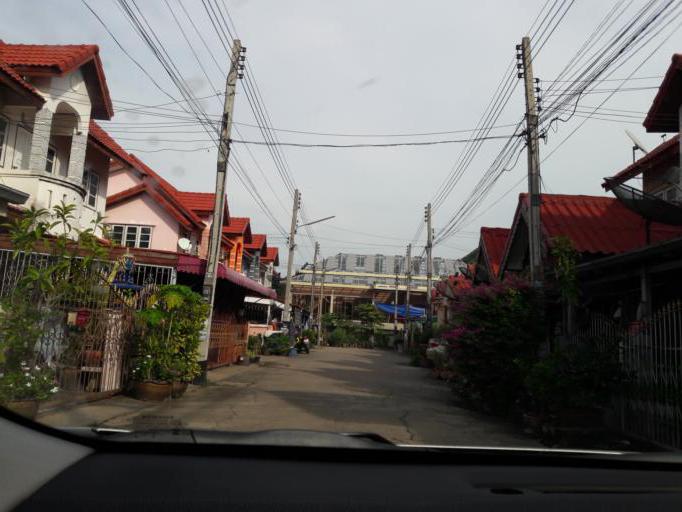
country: TH
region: Ang Thong
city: Ang Thong
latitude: 14.5849
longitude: 100.4448
